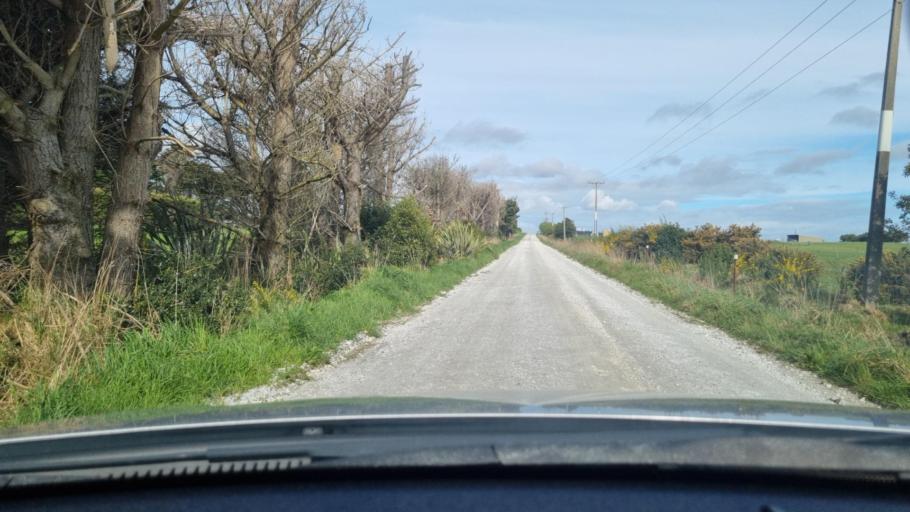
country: NZ
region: Southland
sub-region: Invercargill City
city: Invercargill
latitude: -46.4510
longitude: 168.3808
